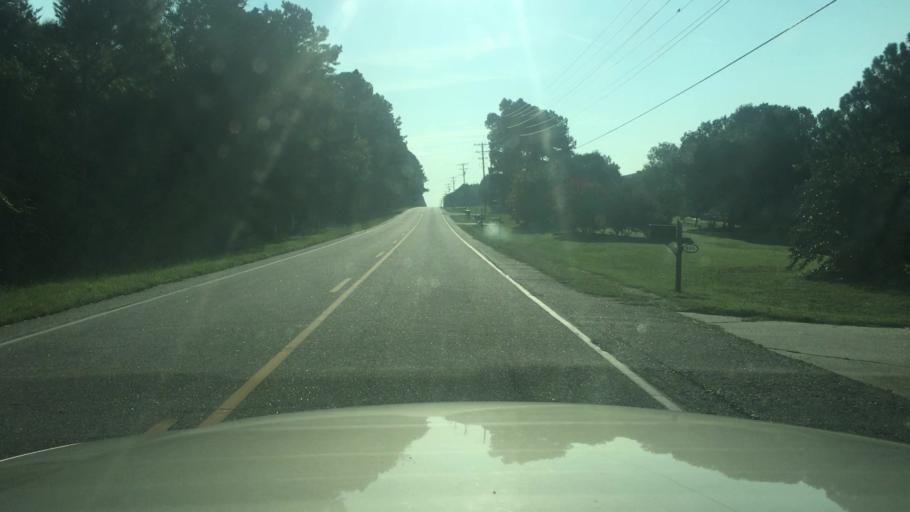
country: US
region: North Carolina
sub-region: Harnett County
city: Walkertown
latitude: 35.2072
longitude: -78.8752
